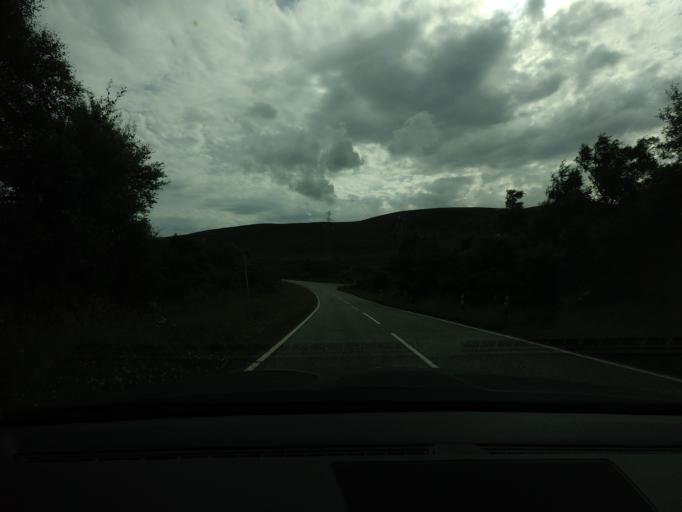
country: GB
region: Scotland
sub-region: Highland
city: Alness
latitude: 57.8343
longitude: -4.2739
